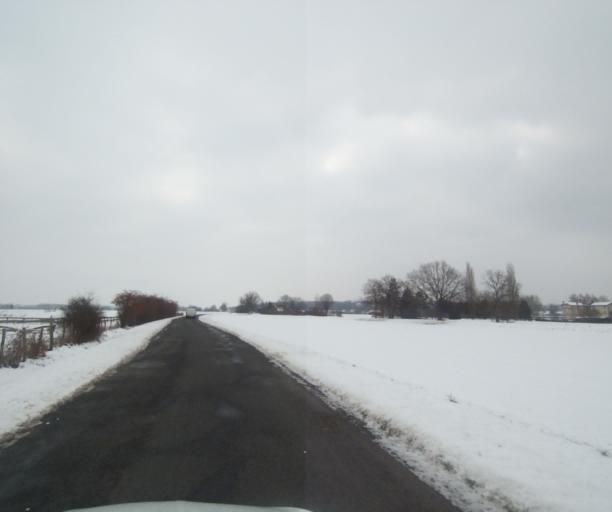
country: FR
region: Champagne-Ardenne
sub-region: Departement de la Haute-Marne
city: Saint-Dizier
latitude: 48.5675
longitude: 4.8916
